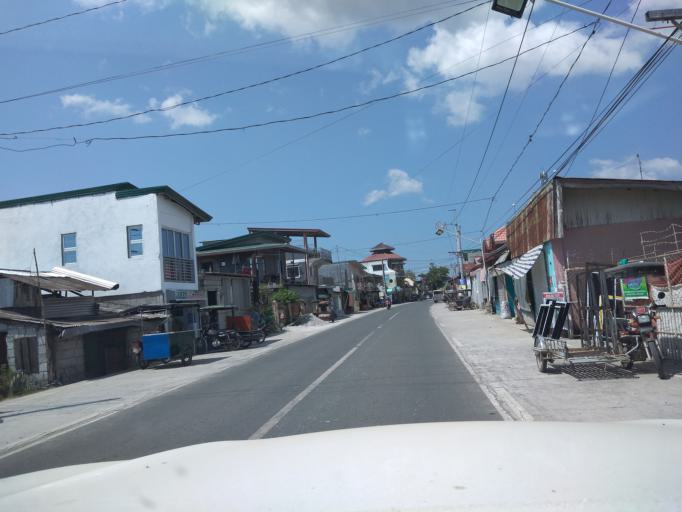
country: PH
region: Central Luzon
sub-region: Province of Pampanga
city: Bahay Pare
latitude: 15.0253
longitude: 120.8830
